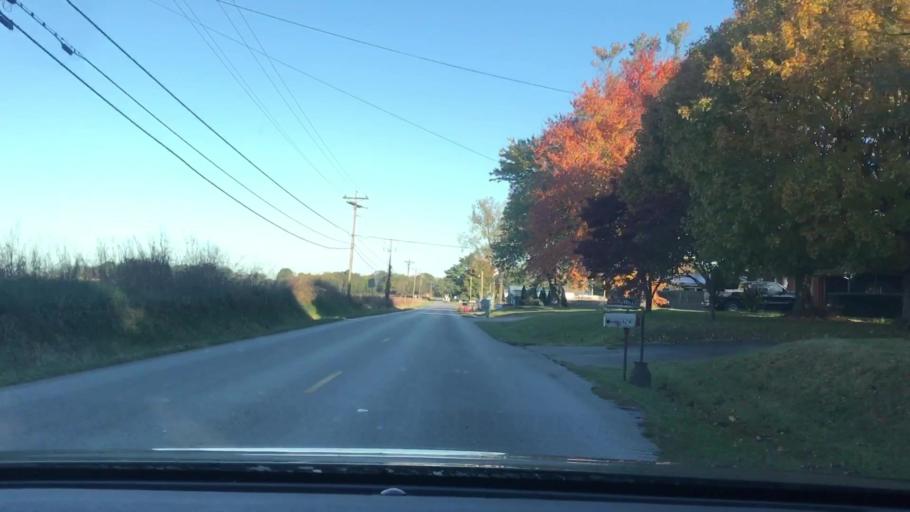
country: US
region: Kentucky
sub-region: Simpson County
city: Franklin
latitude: 36.7400
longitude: -86.5863
